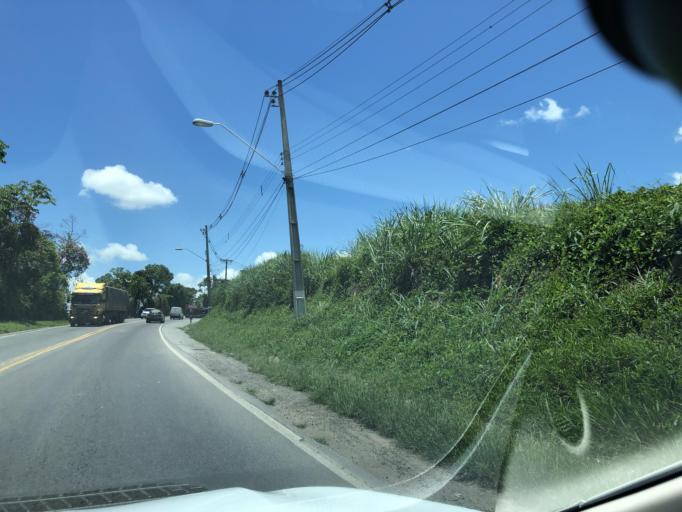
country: BR
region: Santa Catarina
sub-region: Joinville
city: Joinville
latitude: -26.4187
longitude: -48.7786
